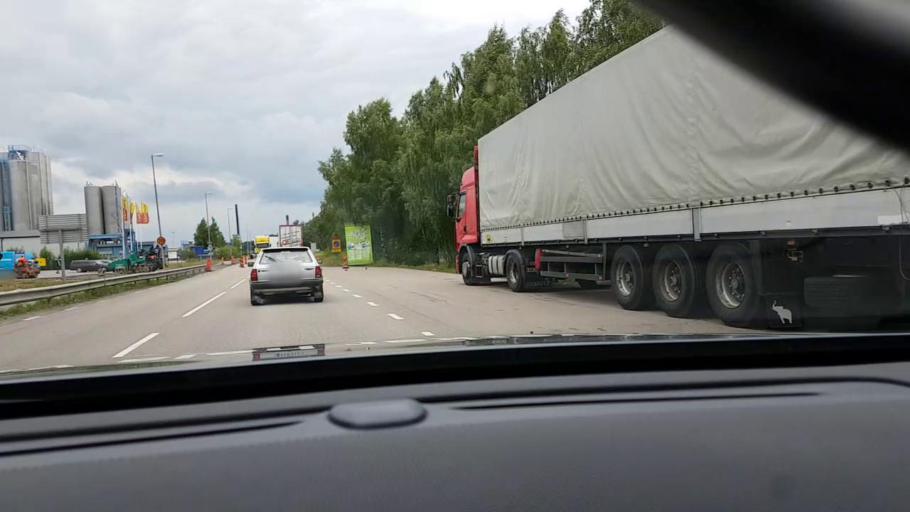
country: SE
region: Skane
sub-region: Hassleholms Kommun
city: Hassleholm
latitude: 56.1563
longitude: 13.8139
